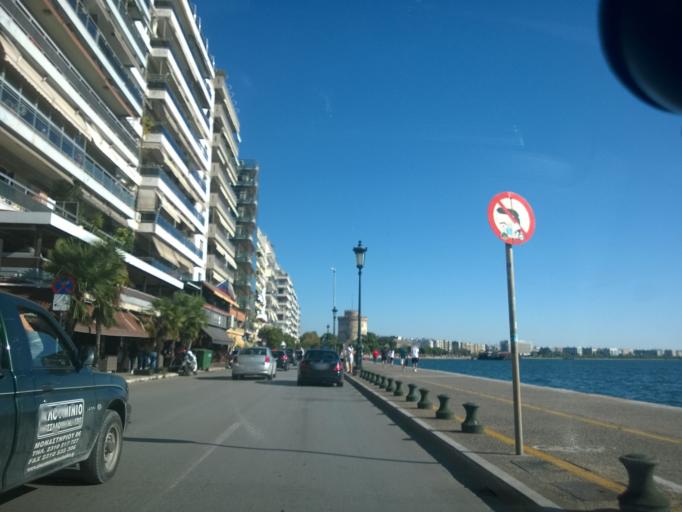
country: GR
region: Central Macedonia
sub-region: Nomos Thessalonikis
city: Agios Pavlos
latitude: 40.6291
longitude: 22.9449
